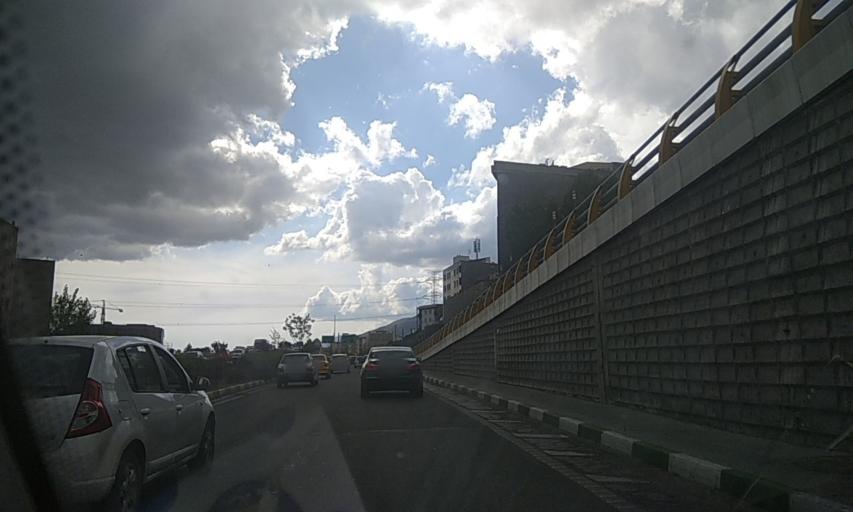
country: IR
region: Tehran
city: Tajrish
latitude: 35.7705
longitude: 51.3223
